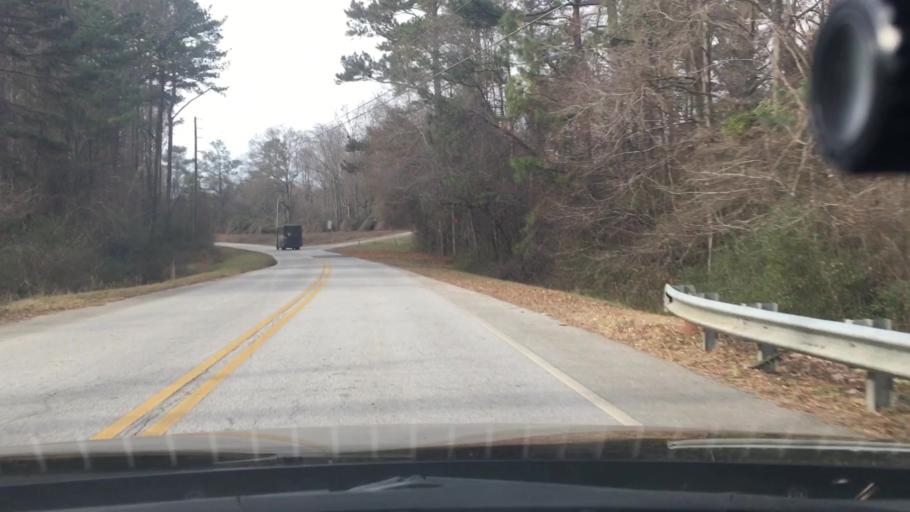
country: US
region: Georgia
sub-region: Spalding County
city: Experiment
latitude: 33.2791
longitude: -84.3761
